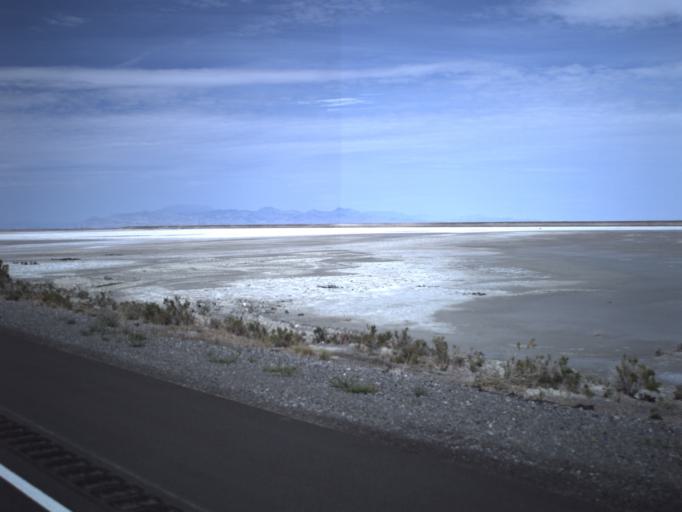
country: US
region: Utah
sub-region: Tooele County
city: Wendover
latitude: 40.7286
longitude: -113.3393
